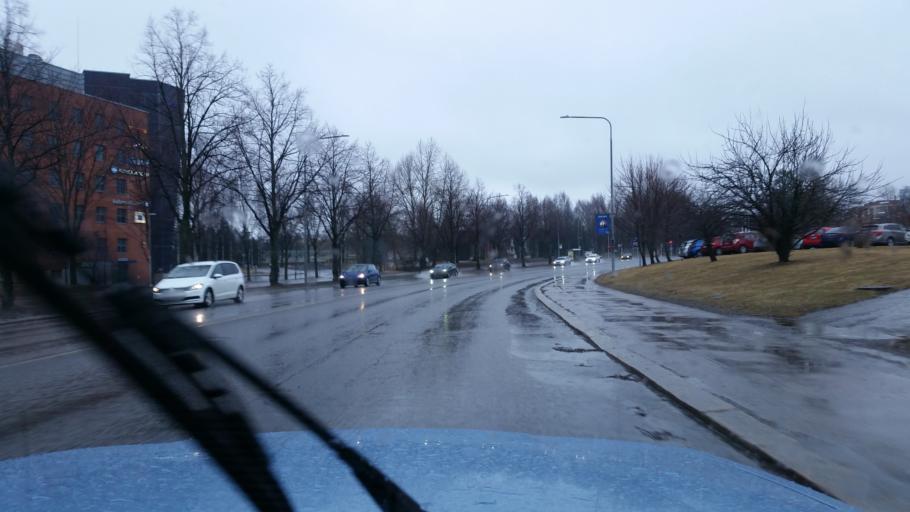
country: FI
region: Pirkanmaa
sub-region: Tampere
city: Tampere
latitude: 61.4849
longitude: 23.7630
